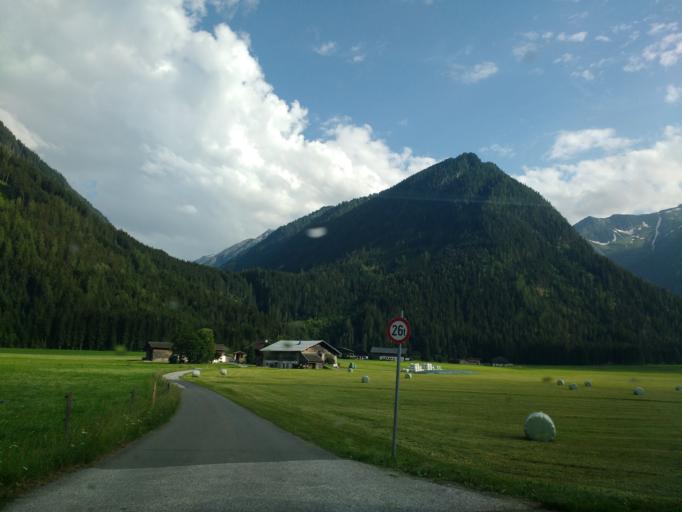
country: AT
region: Salzburg
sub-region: Politischer Bezirk Zell am See
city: Neukirchen am Grossvenediger
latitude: 47.2418
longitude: 12.2609
